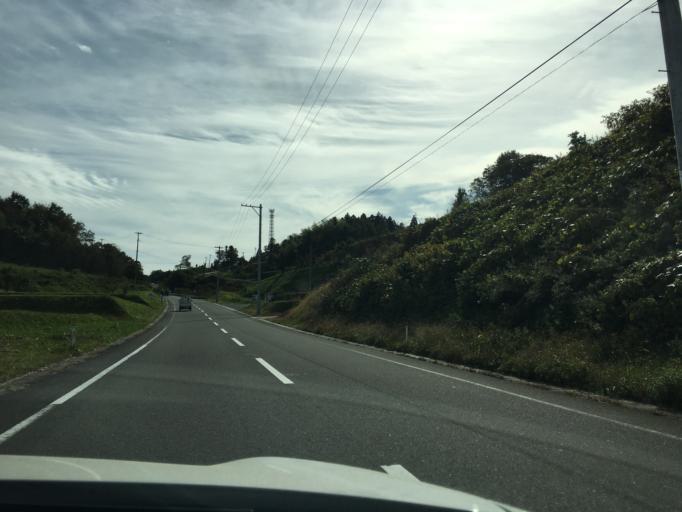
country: JP
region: Fukushima
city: Nihommatsu
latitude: 37.5583
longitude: 140.4995
